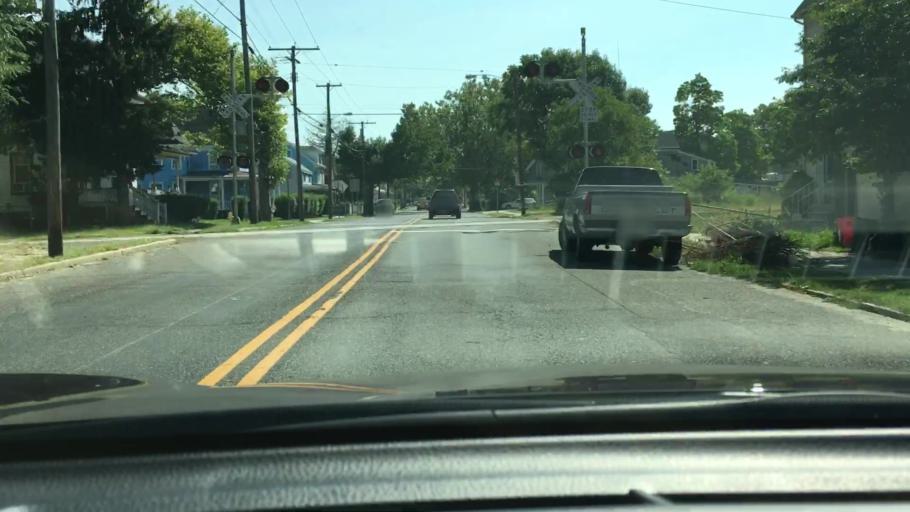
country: US
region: New Jersey
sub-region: Cumberland County
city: Millville
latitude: 39.3953
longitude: -75.0321
